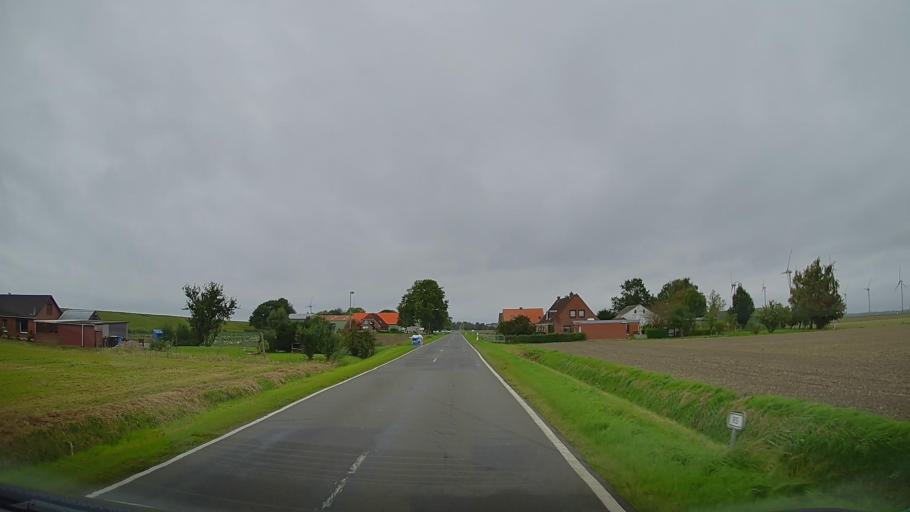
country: DE
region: Schleswig-Holstein
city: Neufeld
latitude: 53.9108
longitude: 9.0057
